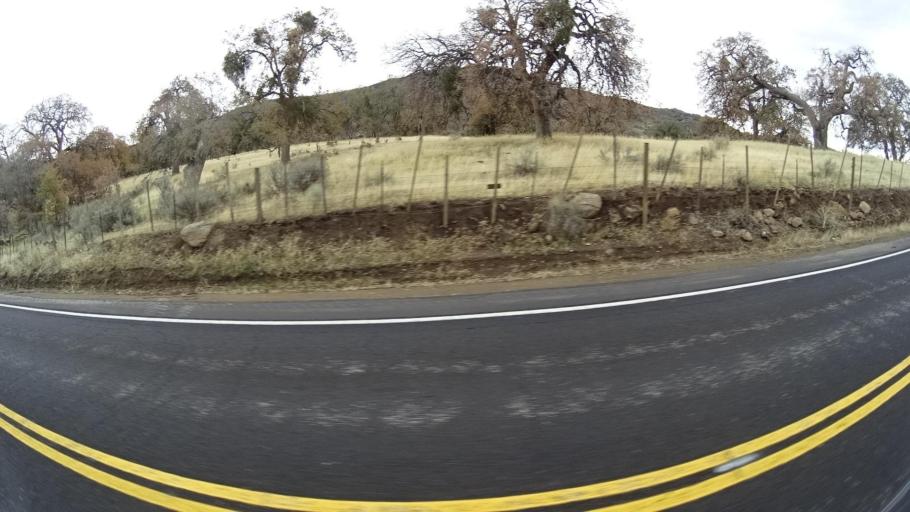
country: US
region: California
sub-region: Kern County
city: Stallion Springs
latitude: 35.0948
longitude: -118.5799
